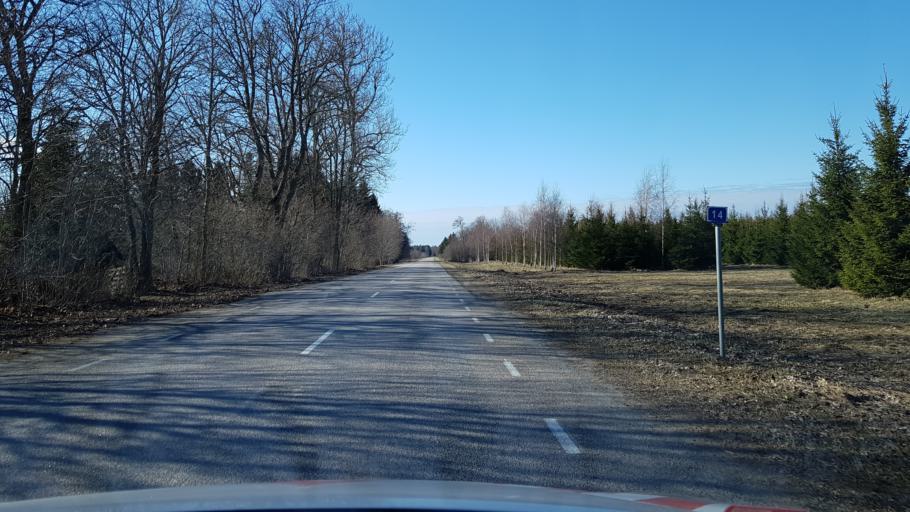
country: EE
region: Laeaene-Virumaa
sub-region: Haljala vald
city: Haljala
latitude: 59.5097
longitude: 26.1073
